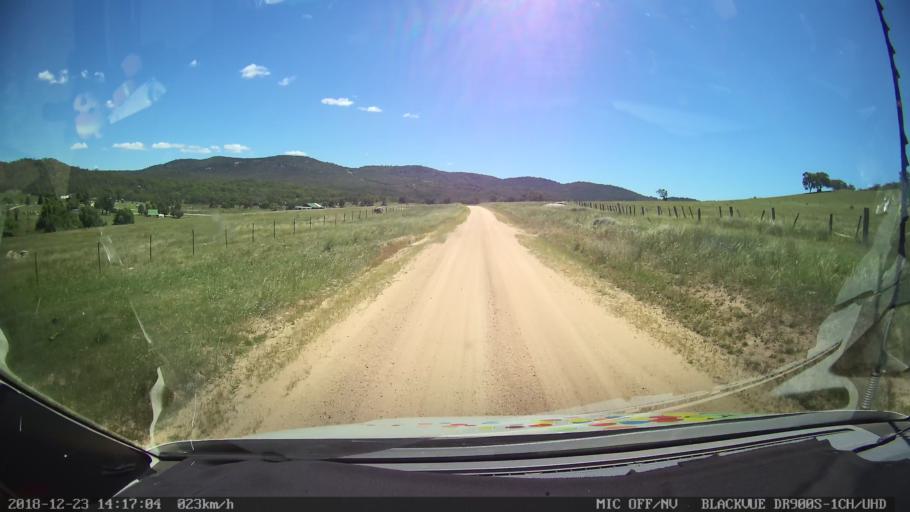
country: AU
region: New South Wales
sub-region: Tamworth Municipality
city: Manilla
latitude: -30.6605
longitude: 151.0135
